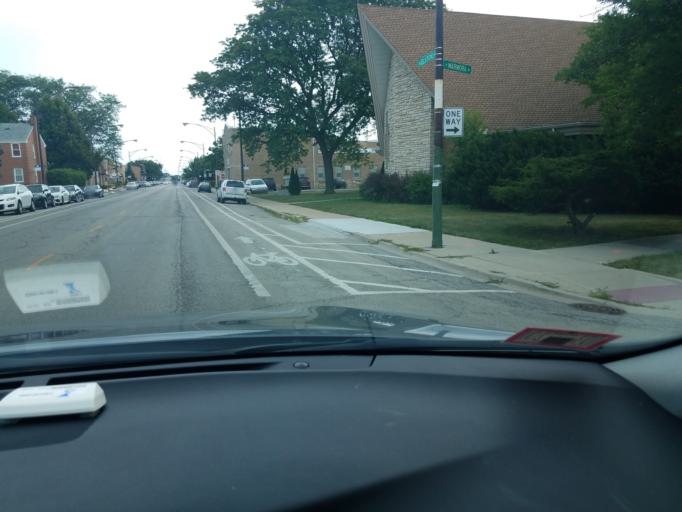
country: US
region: Illinois
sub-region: Cook County
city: Harwood Heights
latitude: 41.9878
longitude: -87.7738
